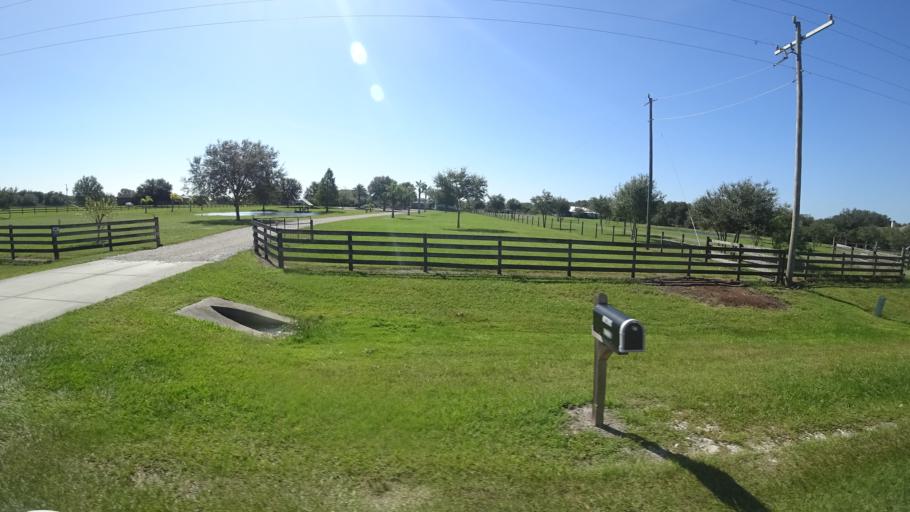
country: US
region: Florida
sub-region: Sarasota County
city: Lake Sarasota
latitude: 27.2888
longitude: -82.2204
